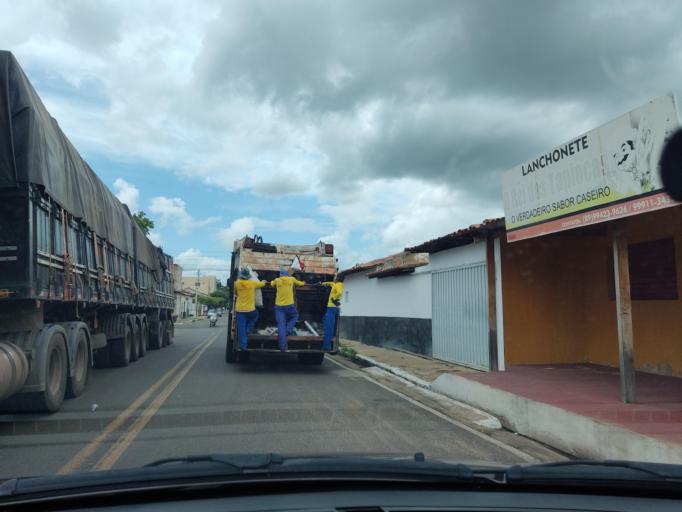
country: BR
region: Piaui
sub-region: Valenca Do Piaui
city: Valenca do Piaui
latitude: -6.4017
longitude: -41.7400
